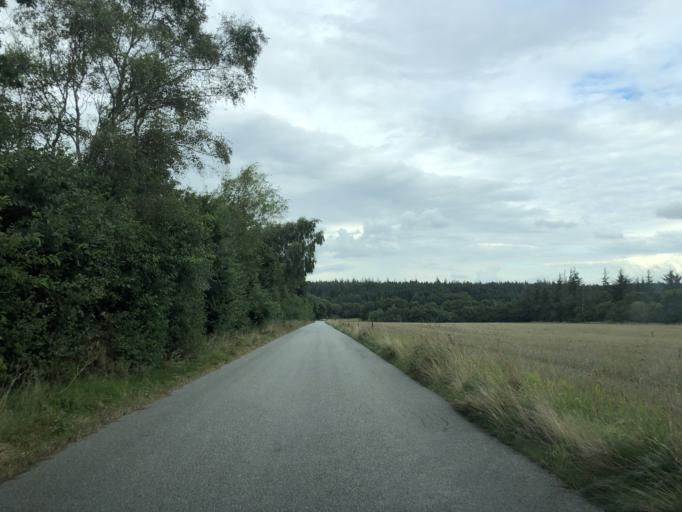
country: DK
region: Central Jutland
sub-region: Holstebro Kommune
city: Ulfborg
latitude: 56.1983
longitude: 8.4237
